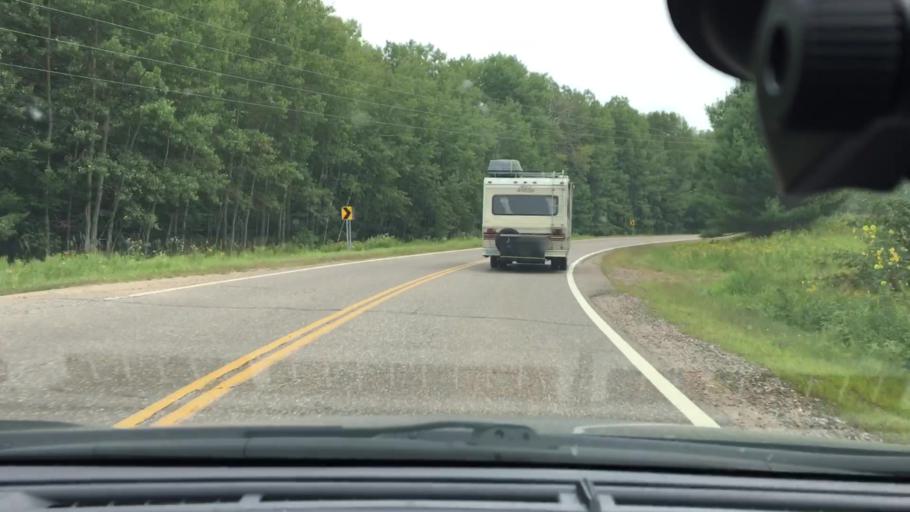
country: US
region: Minnesota
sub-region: Aitkin County
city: Aitkin
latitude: 46.4049
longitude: -93.7913
